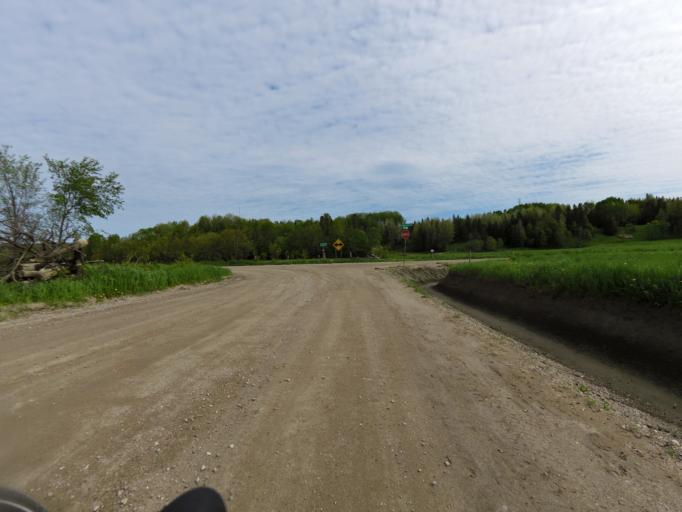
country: CA
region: Quebec
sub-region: Outaouais
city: Wakefield
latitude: 45.7289
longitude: -75.8972
